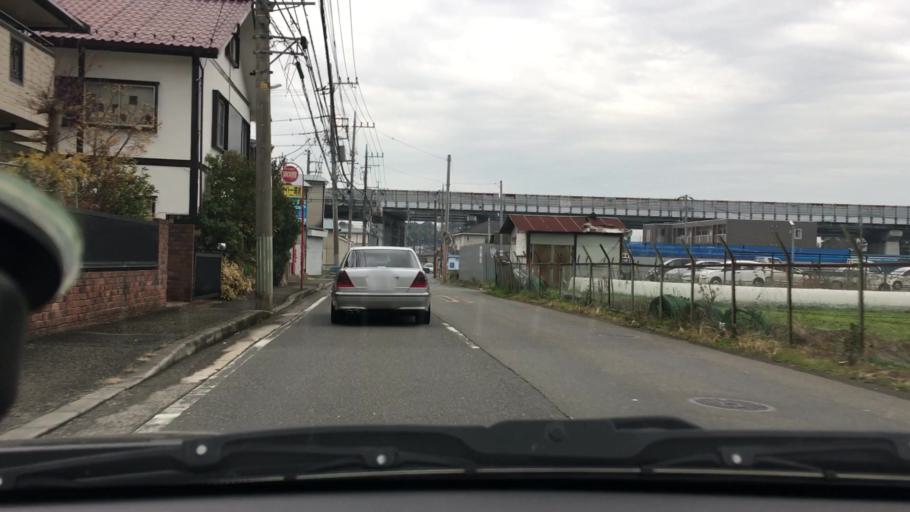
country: JP
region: Kanagawa
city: Yokohama
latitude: 35.5297
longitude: 139.5955
